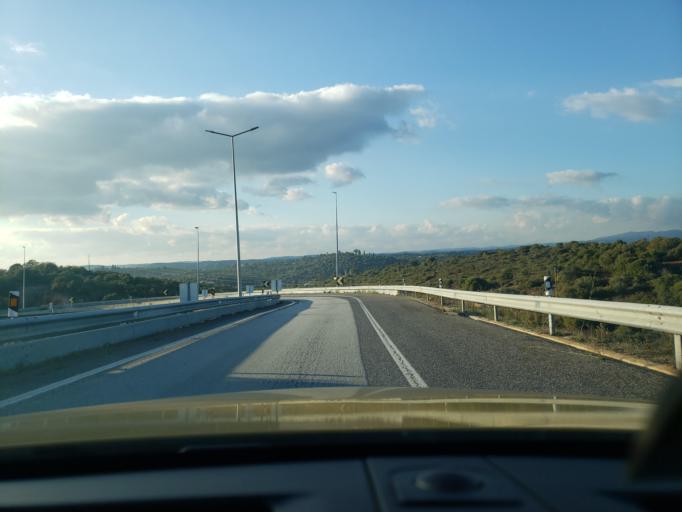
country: PT
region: Faro
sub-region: Portimao
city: Portimao
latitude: 37.1767
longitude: -8.5666
